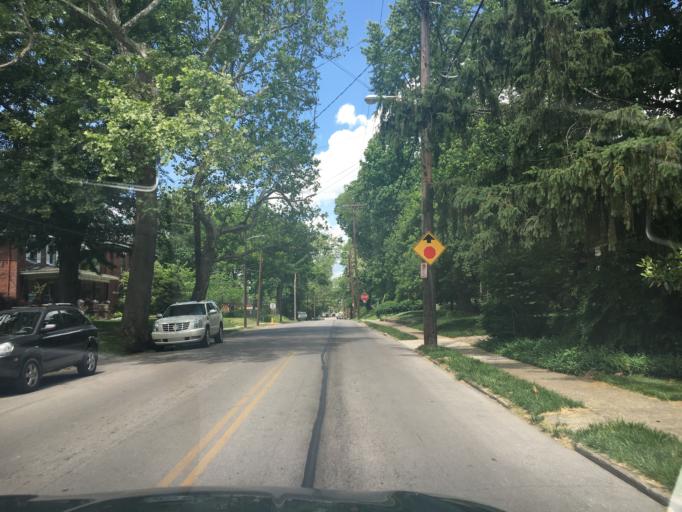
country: US
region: Kentucky
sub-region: Fayette County
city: Mount Vernon
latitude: 38.0572
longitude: -84.4899
